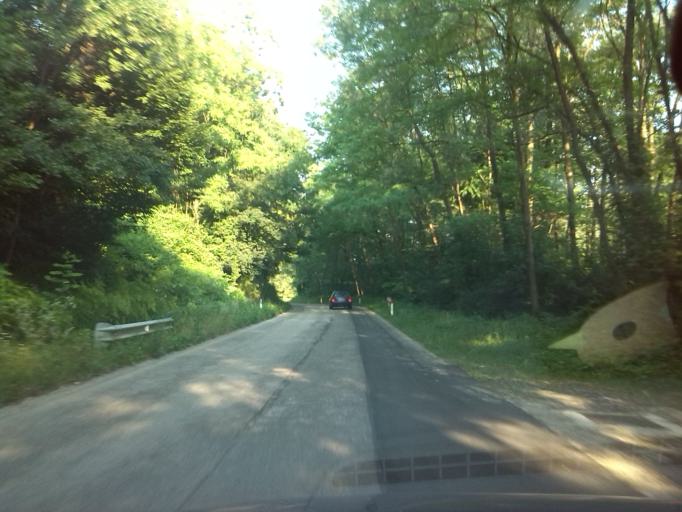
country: IT
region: Friuli Venezia Giulia
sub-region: Provincia di Udine
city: Prepotto
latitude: 46.0473
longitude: 13.4658
